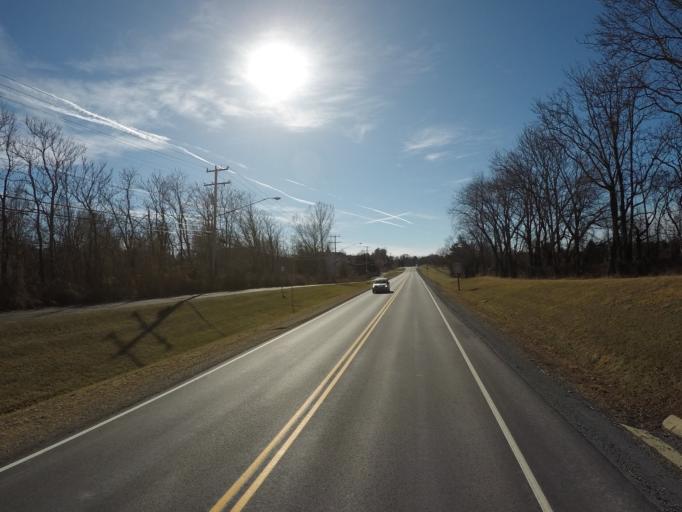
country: US
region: Virginia
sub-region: Loudoun County
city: Leesburg
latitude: 39.1250
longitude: -77.5586
